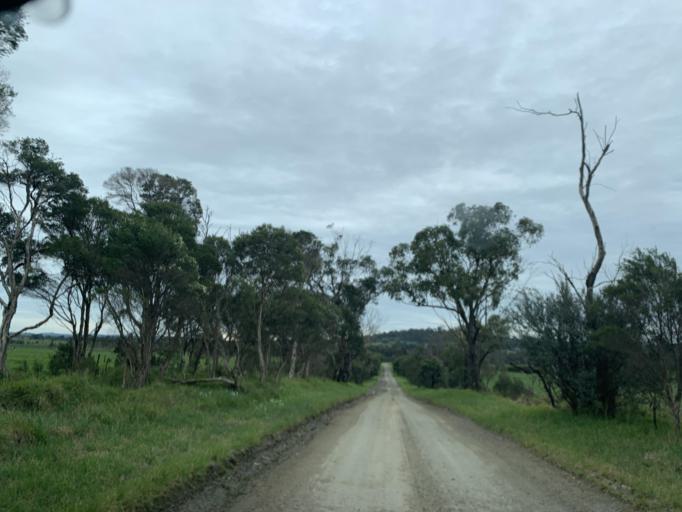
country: AU
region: Victoria
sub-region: Cardinia
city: Garfield
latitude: -38.0949
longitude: 145.6419
